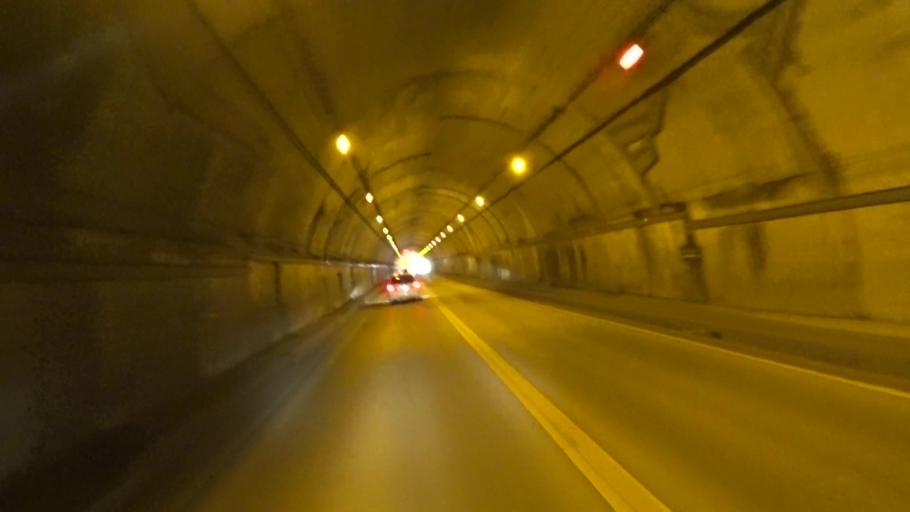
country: JP
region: Kyoto
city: Miyazu
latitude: 35.4433
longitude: 135.0711
